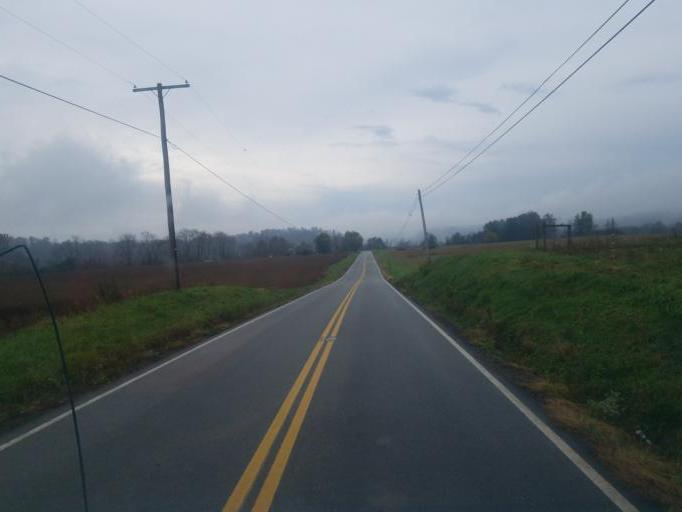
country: US
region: Ohio
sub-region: Morgan County
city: McConnelsville
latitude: 39.5618
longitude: -81.7838
